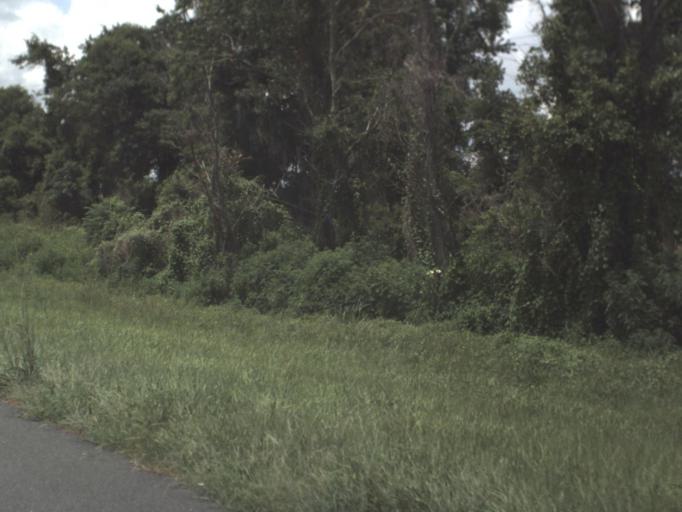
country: US
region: Florida
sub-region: Suwannee County
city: Wellborn
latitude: 30.3948
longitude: -82.8296
